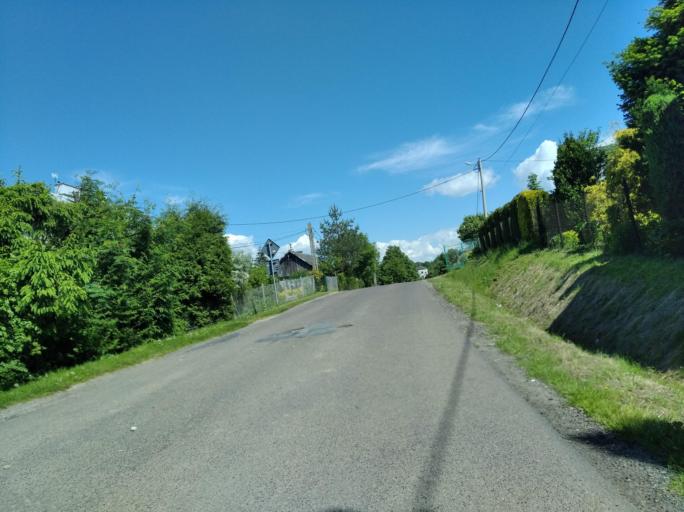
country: PL
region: Subcarpathian Voivodeship
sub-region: Powiat jasielski
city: Tarnowiec
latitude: 49.7123
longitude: 21.6013
